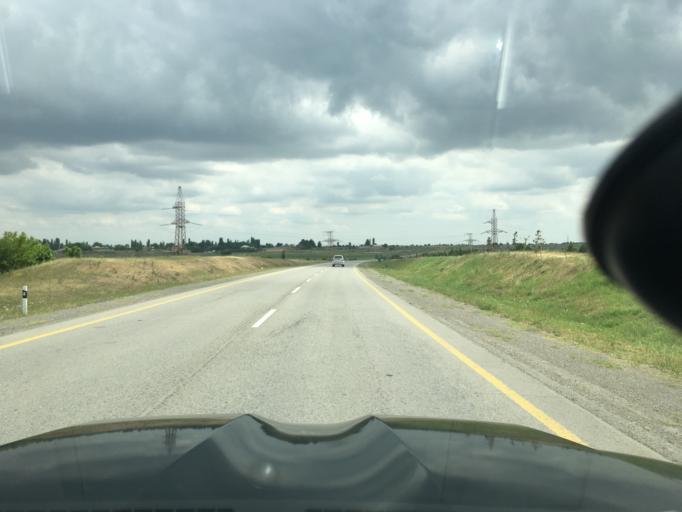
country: AZ
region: Tovuz
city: Qaraxanli
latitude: 41.0292
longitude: 45.6132
